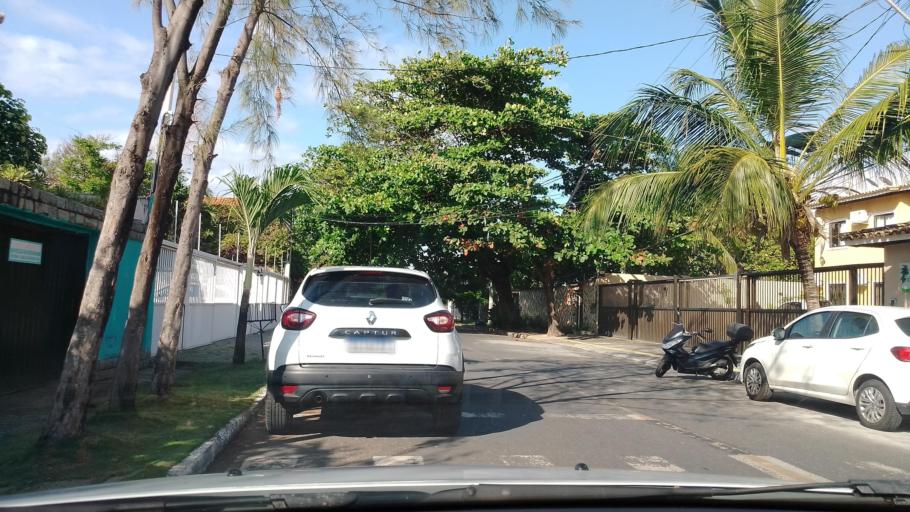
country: BR
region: Bahia
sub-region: Lauro De Freitas
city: Lauro de Freitas
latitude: -12.9409
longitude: -38.3340
